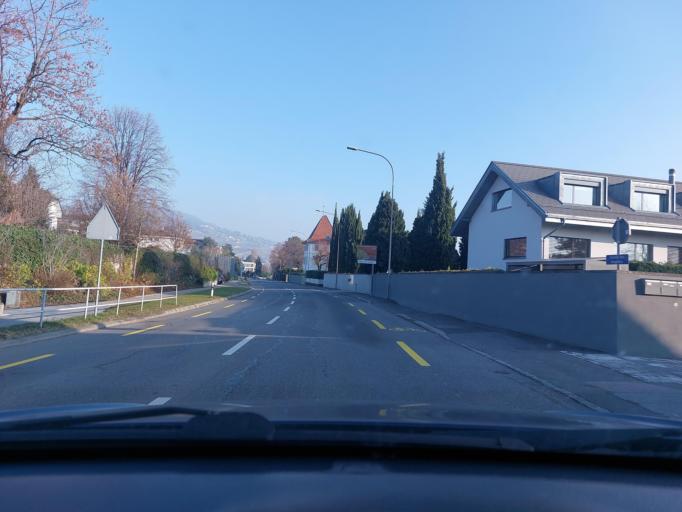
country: CH
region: Vaud
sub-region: Lavaux-Oron District
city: Paudex
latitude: 46.5052
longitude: 6.6722
